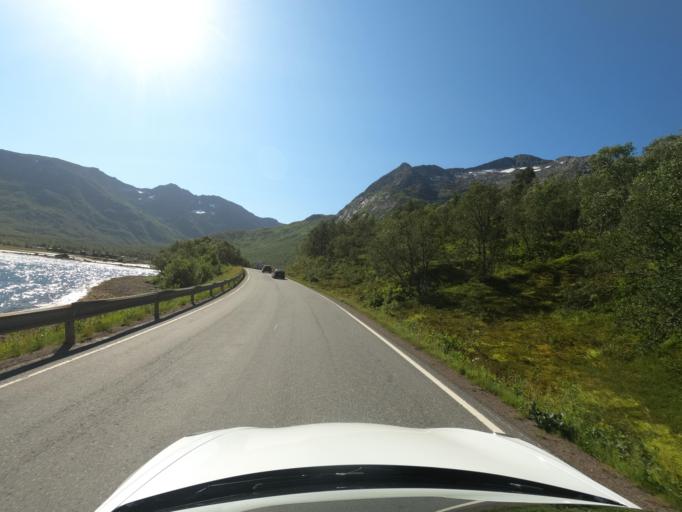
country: NO
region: Nordland
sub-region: Lodingen
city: Lodingen
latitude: 68.5365
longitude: 15.7223
